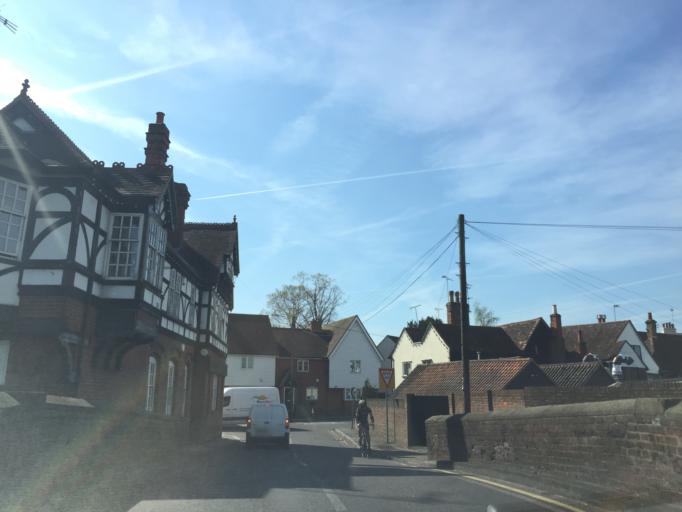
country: GB
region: England
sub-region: Essex
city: Theydon Bois
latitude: 51.6518
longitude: 0.1183
